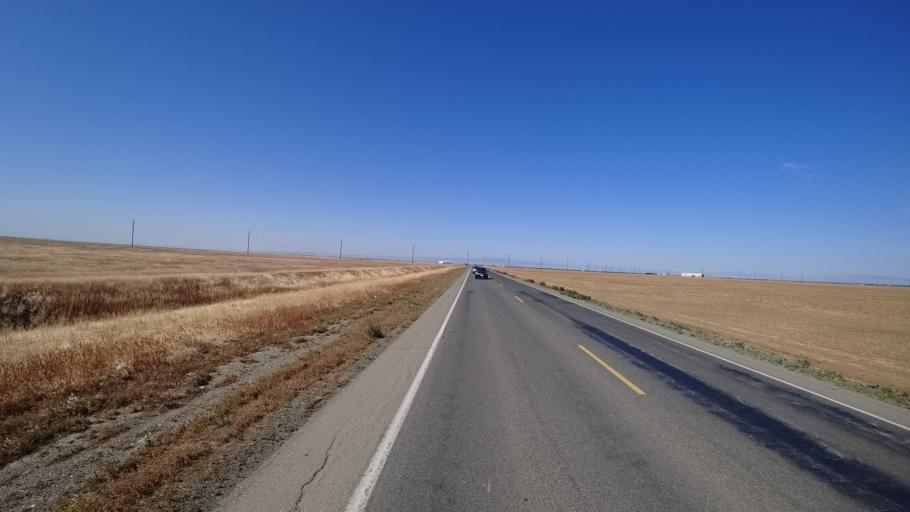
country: US
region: California
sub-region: Kings County
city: Lemoore Station
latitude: 36.2295
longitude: -119.8941
